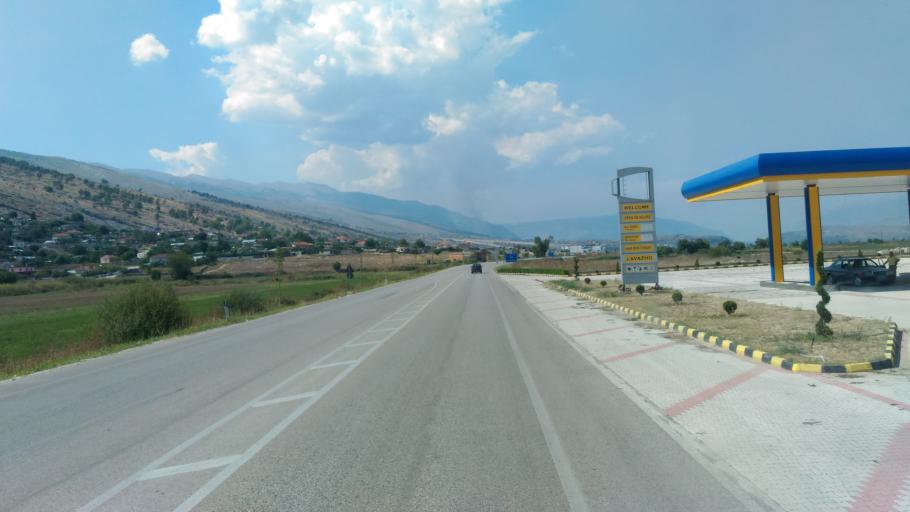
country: AL
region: Gjirokaster
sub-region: Rrethi i Gjirokastres
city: Dervician
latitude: 40.0147
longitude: 20.1986
